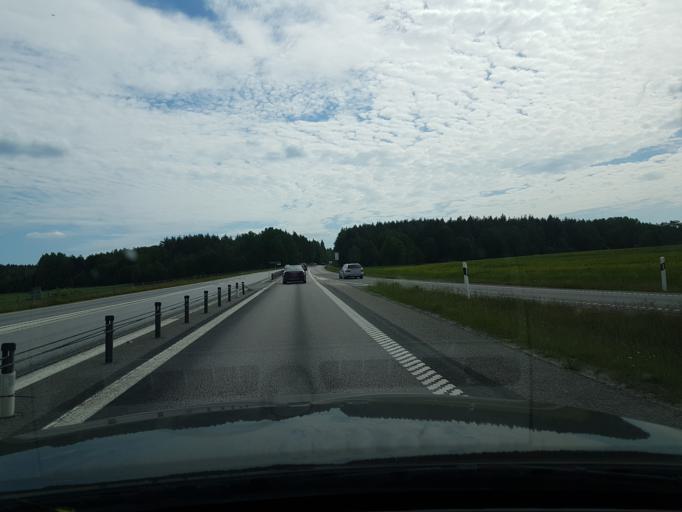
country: SE
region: Stockholm
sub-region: Osterakers Kommun
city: Akersberga
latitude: 59.5572
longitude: 18.2311
